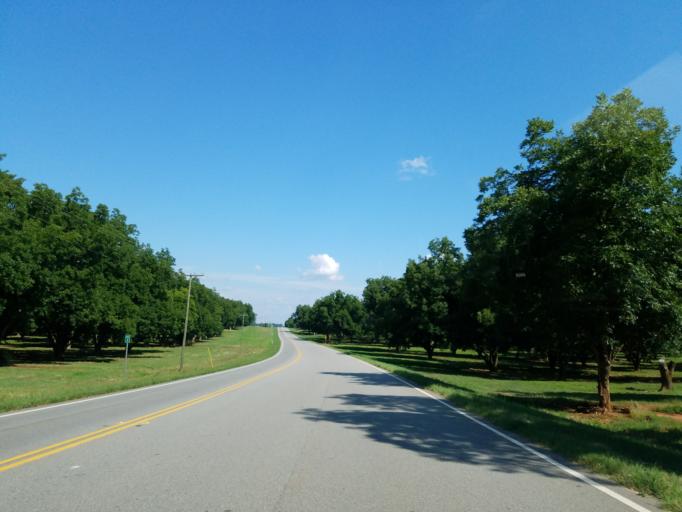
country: US
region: Georgia
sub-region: Peach County
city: Fort Valley
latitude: 32.6196
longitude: -83.9635
